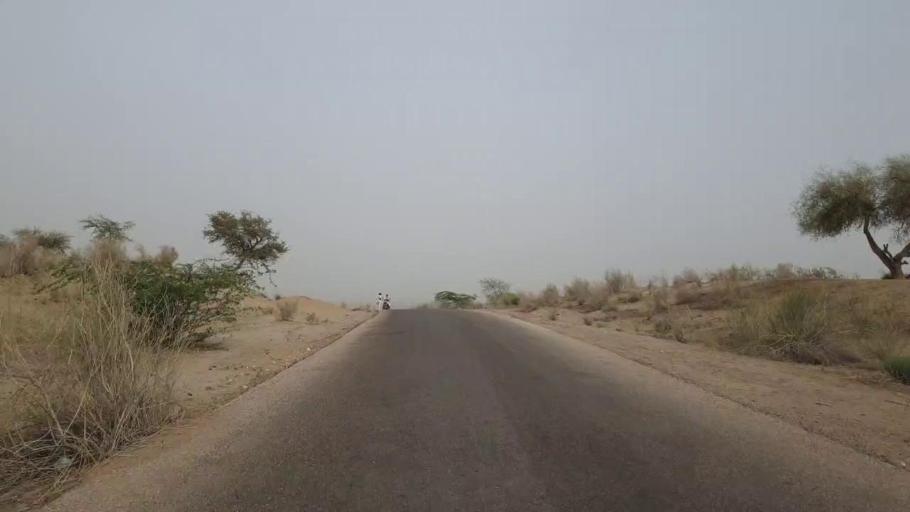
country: PK
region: Sindh
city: Islamkot
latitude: 24.5834
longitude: 70.2984
